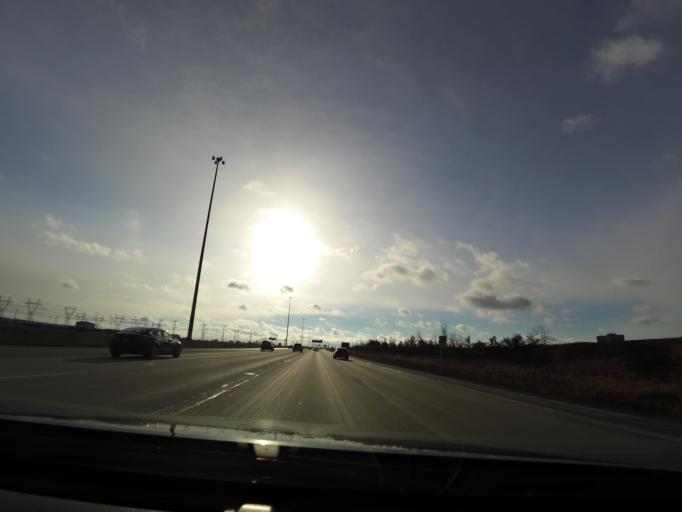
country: CA
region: Ontario
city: Brampton
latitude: 43.6621
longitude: -79.7074
